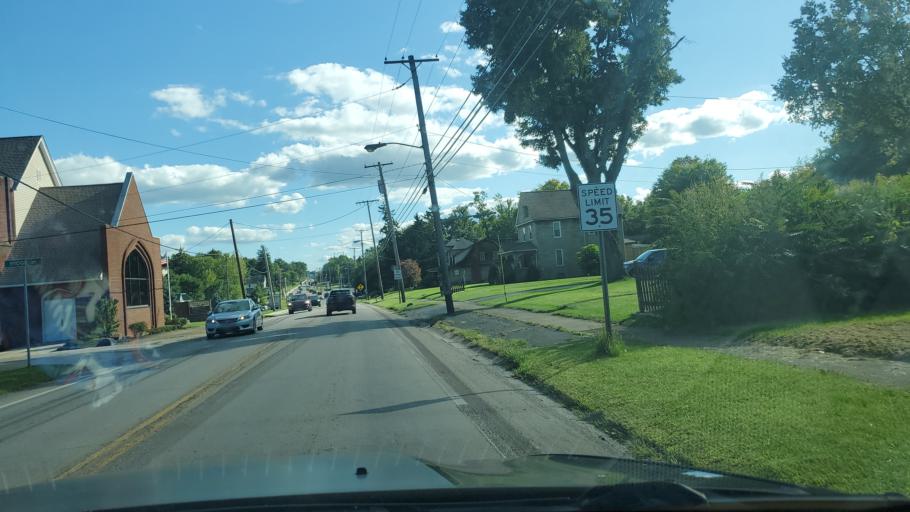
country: US
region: Ohio
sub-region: Trumbull County
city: Mineral Ridge
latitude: 41.1370
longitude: -80.7689
